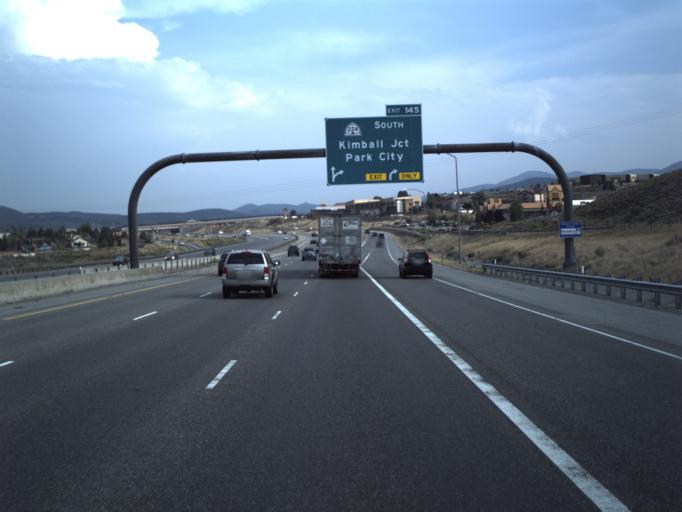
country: US
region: Utah
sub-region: Summit County
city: Snyderville
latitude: 40.7336
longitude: -111.5527
